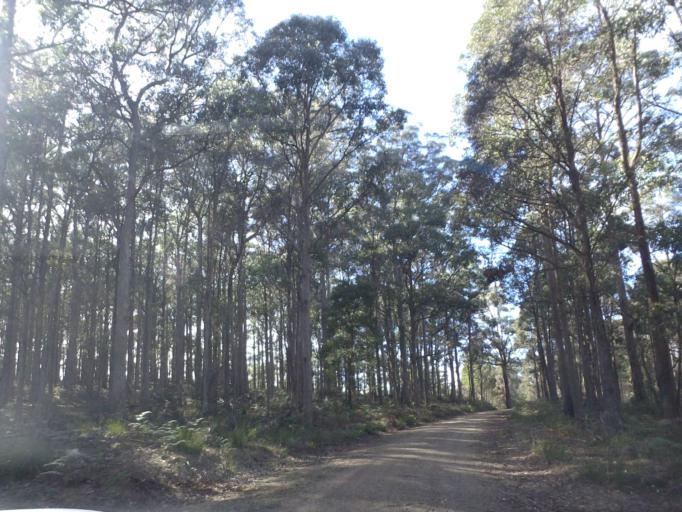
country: AU
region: Victoria
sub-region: Moorabool
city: Bacchus Marsh
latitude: -37.4286
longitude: 144.2339
